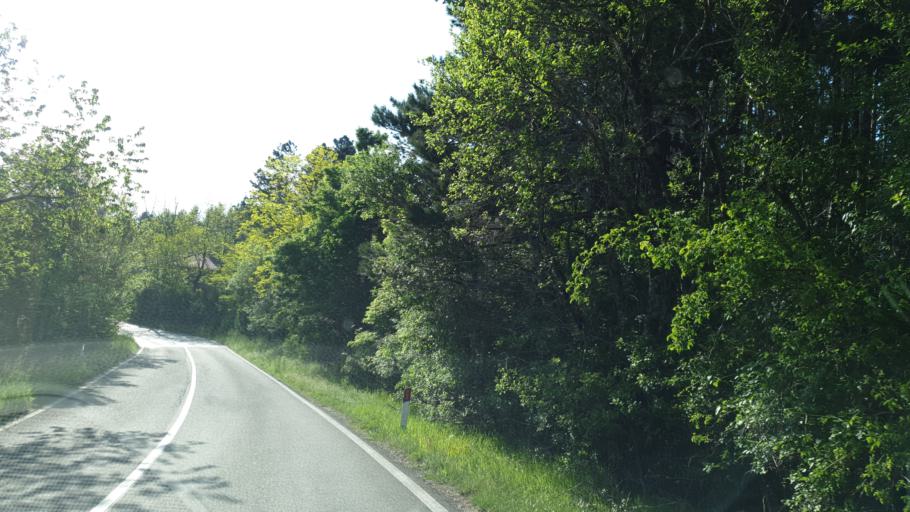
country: IT
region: Tuscany
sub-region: Province of Arezzo
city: Montemignaio
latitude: 43.7878
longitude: 11.6393
